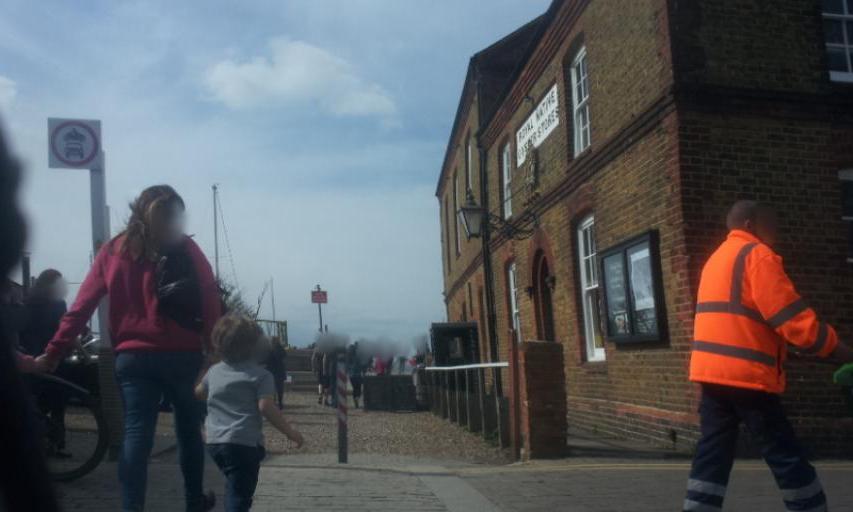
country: GB
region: England
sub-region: Kent
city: Whitstable
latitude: 51.3608
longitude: 1.0236
